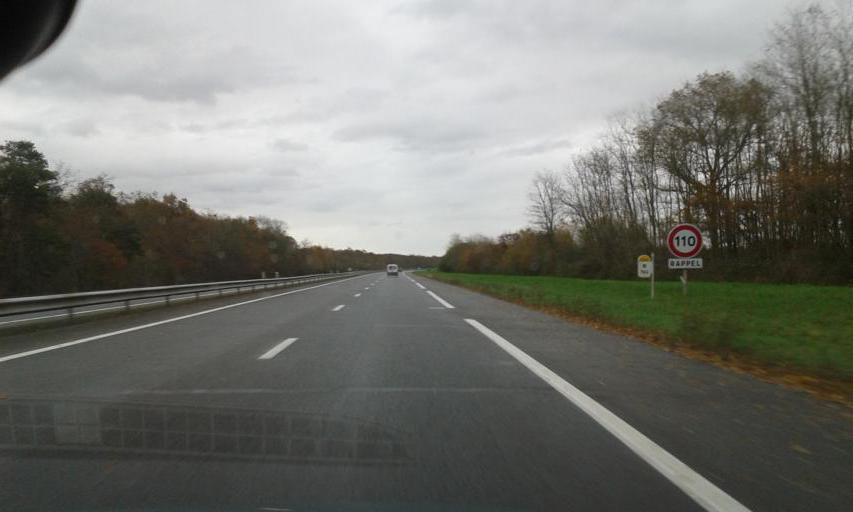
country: FR
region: Centre
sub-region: Departement du Loiret
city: Fay-aux-Loges
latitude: 47.9079
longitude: 2.1761
